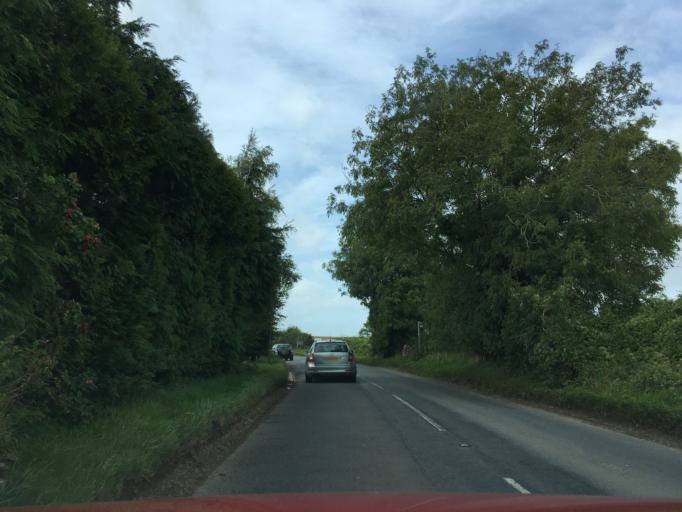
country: GB
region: England
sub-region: Gloucestershire
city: Stonehouse
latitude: 51.7007
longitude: -2.2932
